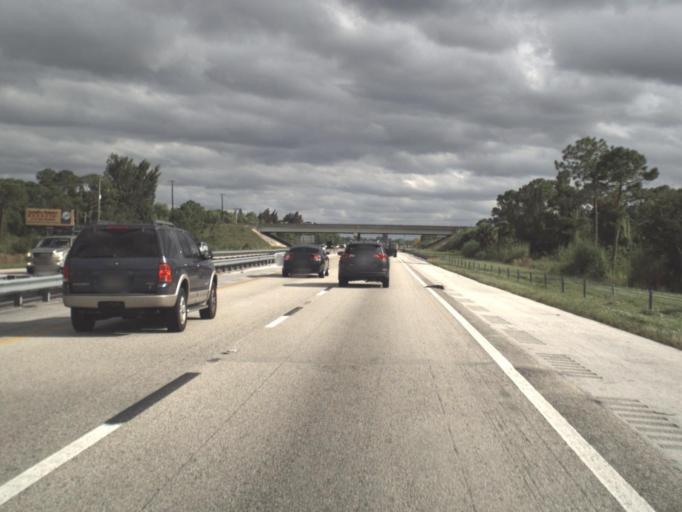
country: US
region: Florida
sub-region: Martin County
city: Palm City
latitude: 27.1070
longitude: -80.2674
